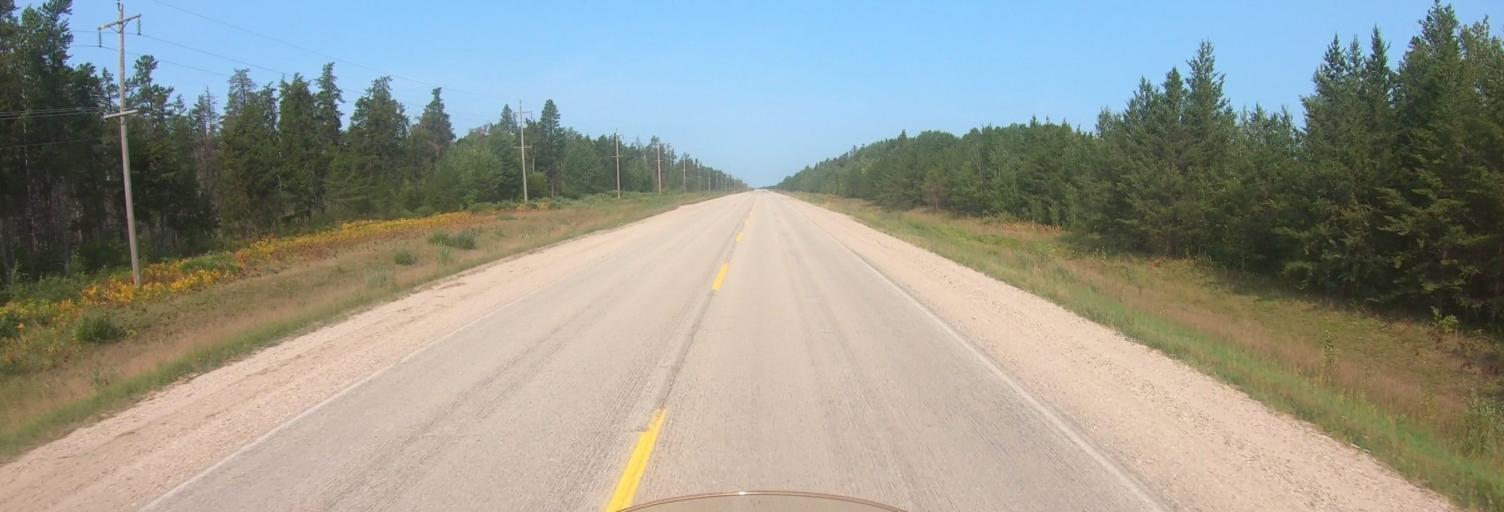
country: US
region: Minnesota
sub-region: Roseau County
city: Roseau
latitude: 49.0778
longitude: -95.8637
